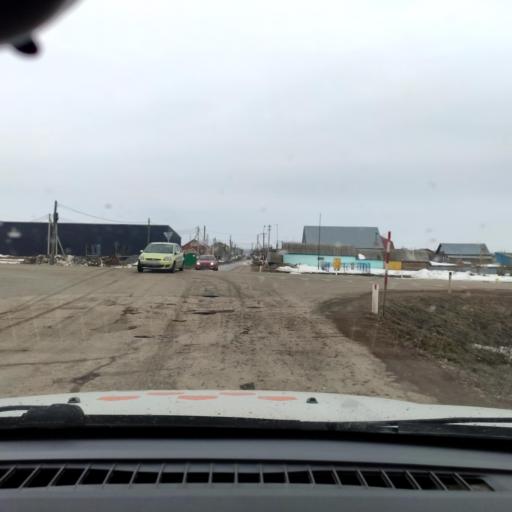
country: RU
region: Bashkortostan
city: Kushnarenkovo
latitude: 55.1057
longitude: 55.3294
